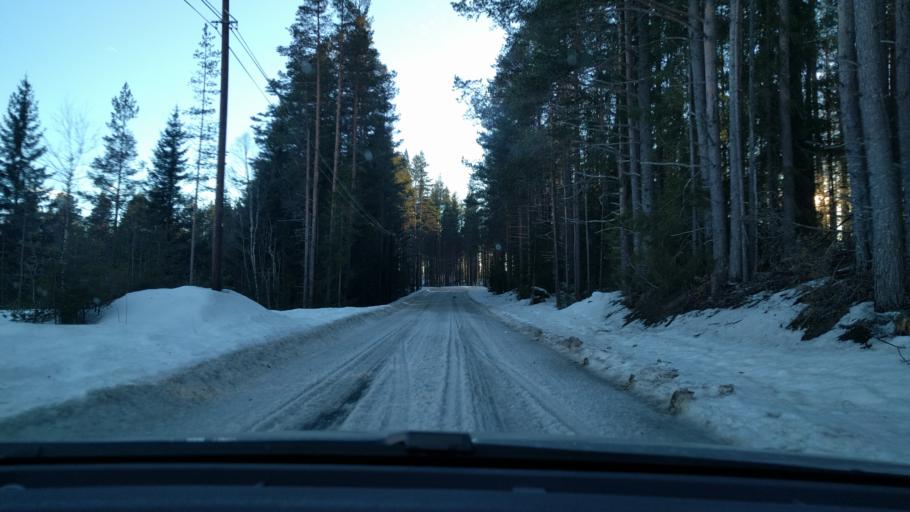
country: NO
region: Hedmark
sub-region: Elverum
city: Elverum
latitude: 60.9961
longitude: 11.7678
